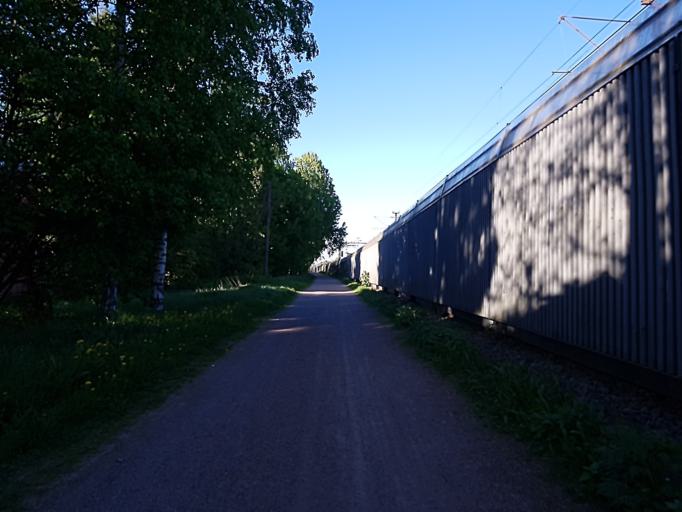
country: FI
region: Uusimaa
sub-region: Helsinki
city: Helsinki
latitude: 60.2251
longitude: 24.9596
